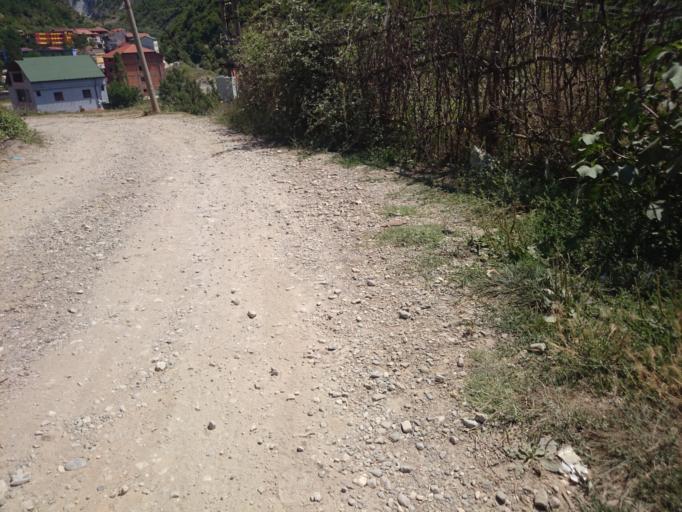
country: AL
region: Diber
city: Peshkopi
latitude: 41.6862
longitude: 20.4451
